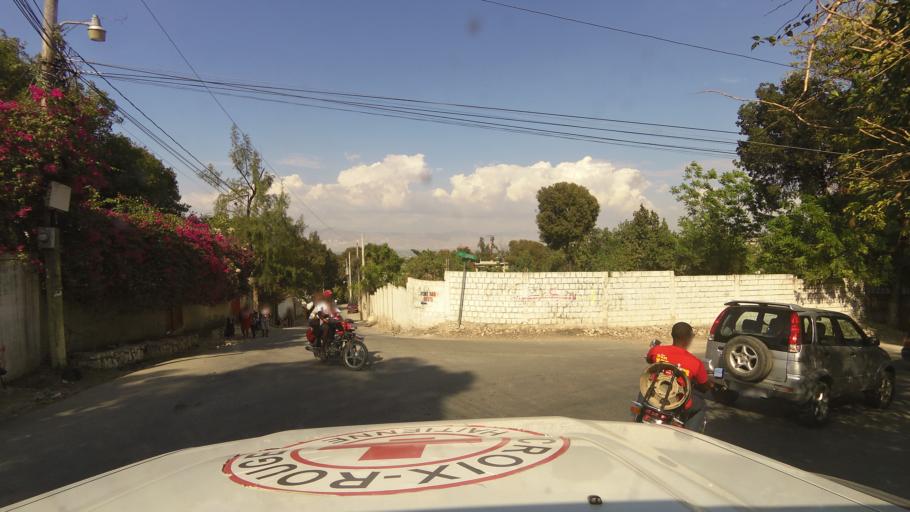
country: HT
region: Ouest
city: Petionville
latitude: 18.5322
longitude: -72.2857
